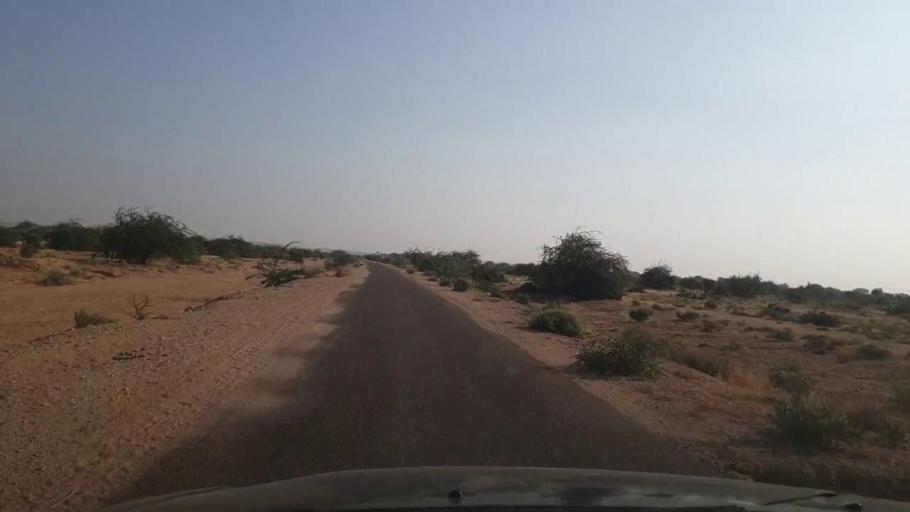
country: PK
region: Sindh
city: Jamshoro
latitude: 25.3395
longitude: 67.8406
